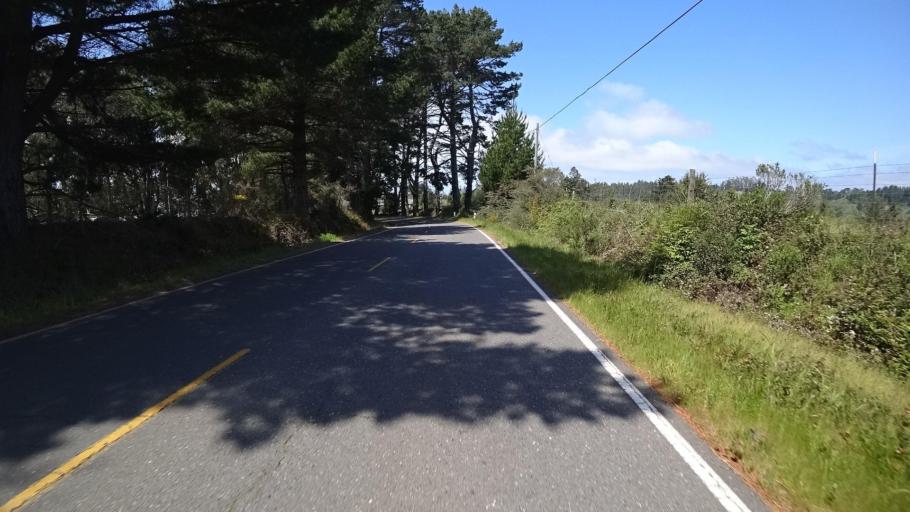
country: US
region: California
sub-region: Humboldt County
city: Fortuna
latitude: 40.6450
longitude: -124.2139
